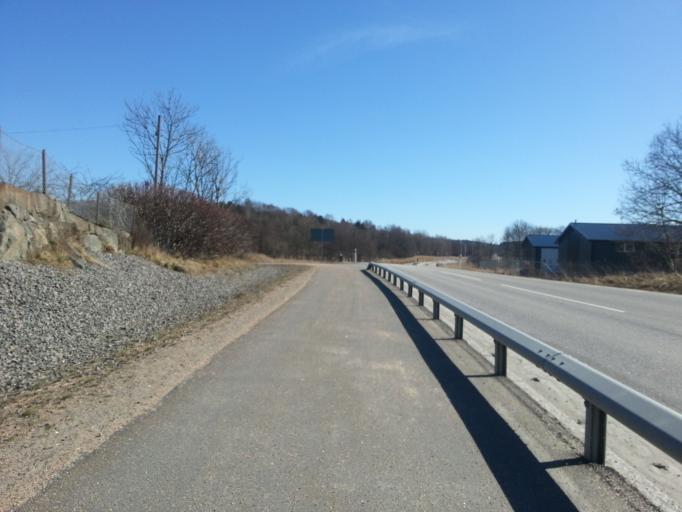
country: SE
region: Vaestra Goetaland
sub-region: Kungalvs Kommun
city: Kungalv
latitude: 57.8970
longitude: 11.9352
